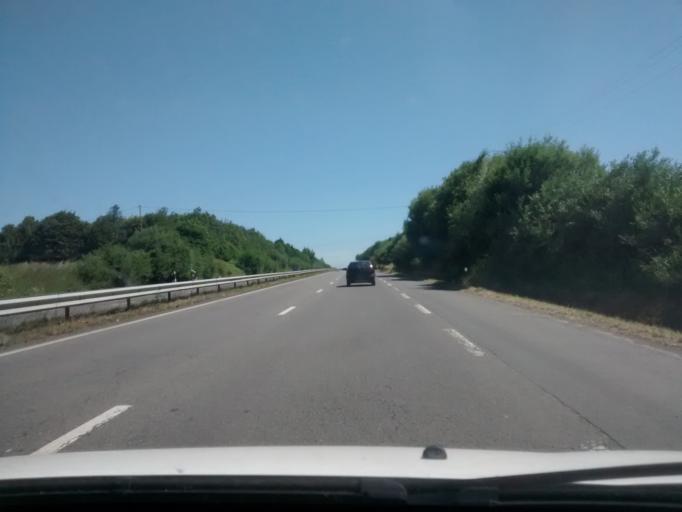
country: FR
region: Brittany
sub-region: Departement d'Ille-et-Vilaine
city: La Meziere
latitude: 48.2289
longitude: -1.7538
